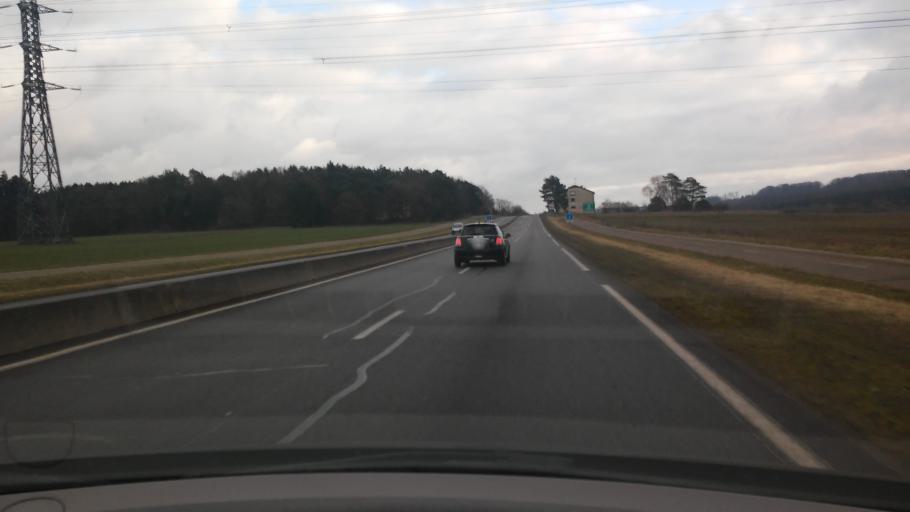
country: FR
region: Lorraine
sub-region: Departement de la Moselle
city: Saint-Avold
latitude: 49.1127
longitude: 6.6730
